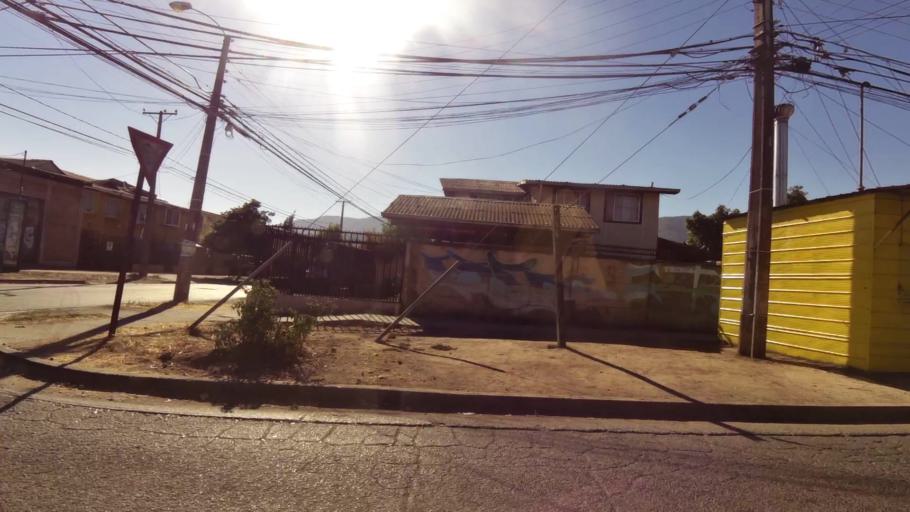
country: CL
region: O'Higgins
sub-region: Provincia de Colchagua
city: Chimbarongo
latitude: -34.5773
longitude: -70.9994
